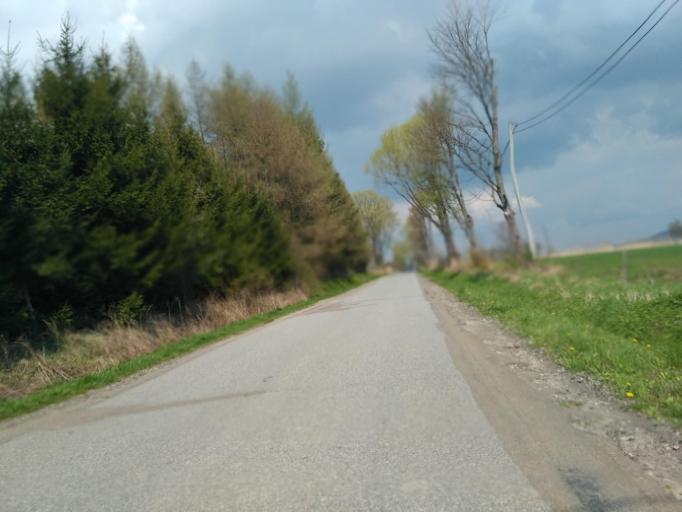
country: PL
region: Subcarpathian Voivodeship
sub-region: Powiat sanocki
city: Nowosielce-Gniewosz
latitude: 49.5677
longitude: 22.1205
